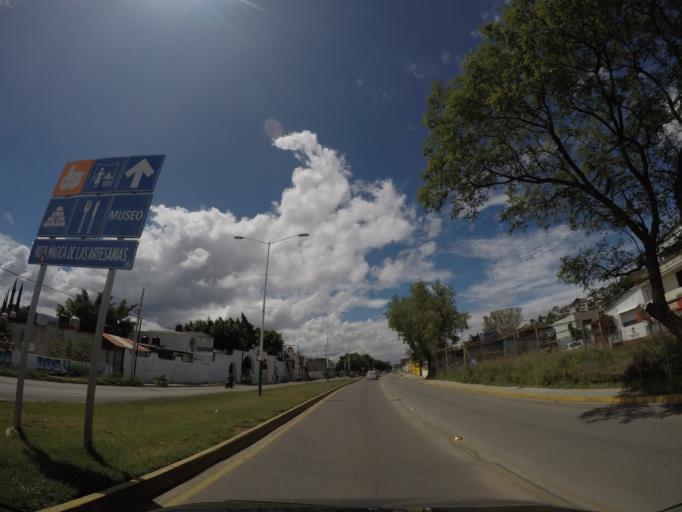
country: MX
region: Oaxaca
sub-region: Santa Cruz Xoxocotlan
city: Santa Cruz Xoxocotlan
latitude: 17.0420
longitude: -96.7294
